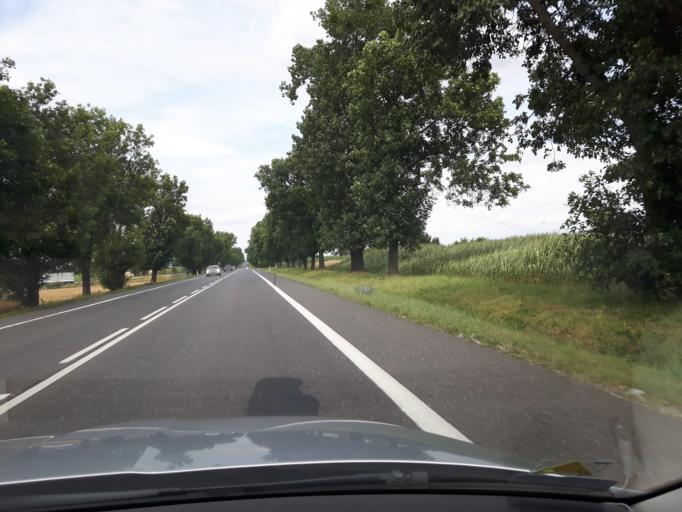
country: PL
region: Masovian Voivodeship
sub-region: Powiat mlawski
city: Wisniewo
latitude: 53.0244
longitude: 20.3361
